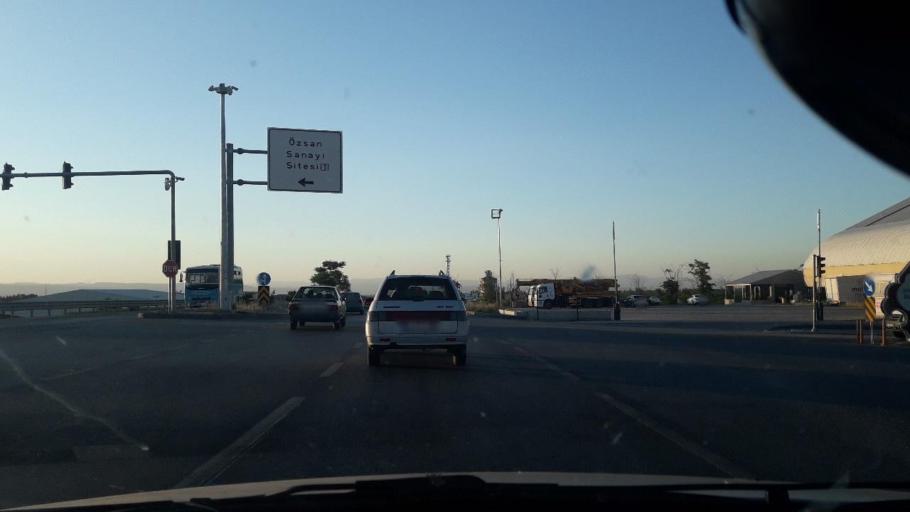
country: TR
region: Malatya
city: Yesilyurt
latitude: 38.3396
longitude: 38.2346
